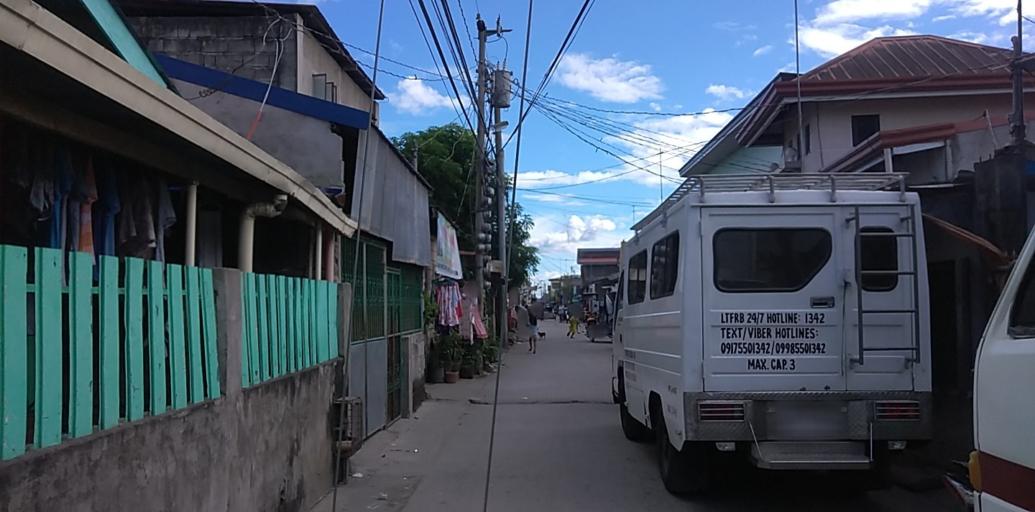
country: PH
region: Central Luzon
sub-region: Province of Pampanga
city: Arayat
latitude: 15.1413
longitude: 120.7690
